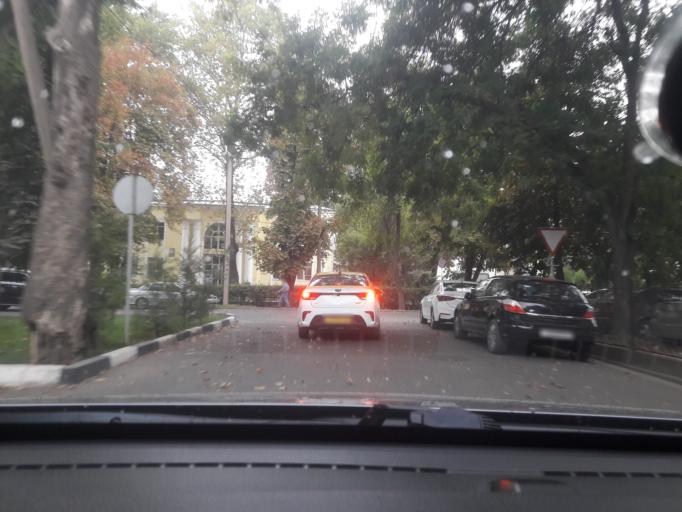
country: TJ
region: Dushanbe
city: Dushanbe
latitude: 38.5663
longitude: 68.7917
